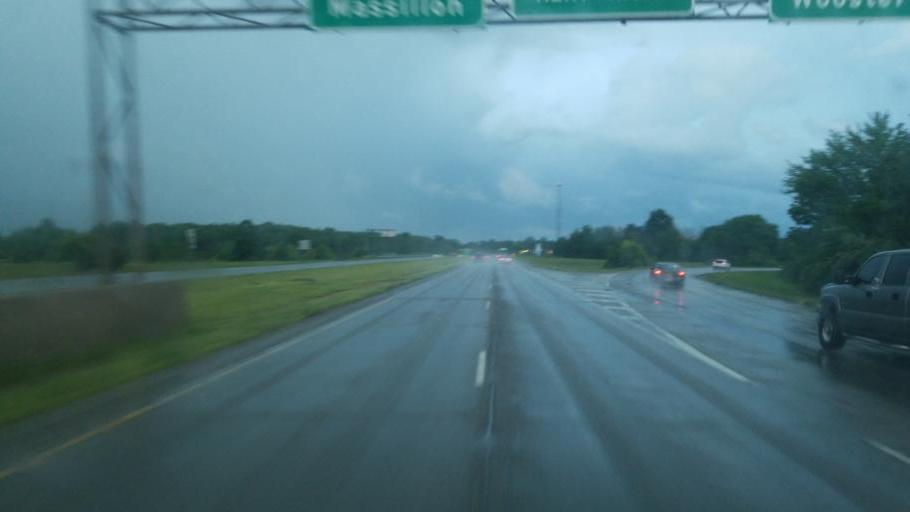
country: US
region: Ohio
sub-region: Summit County
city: Norton
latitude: 40.9966
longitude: -81.6622
